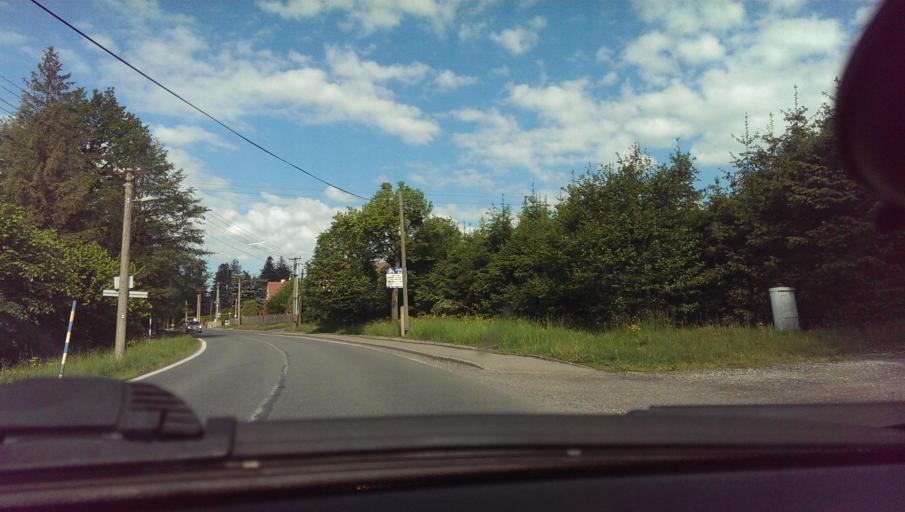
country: CZ
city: Kuncice pod Ondrejnikem
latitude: 49.5388
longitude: 18.2983
